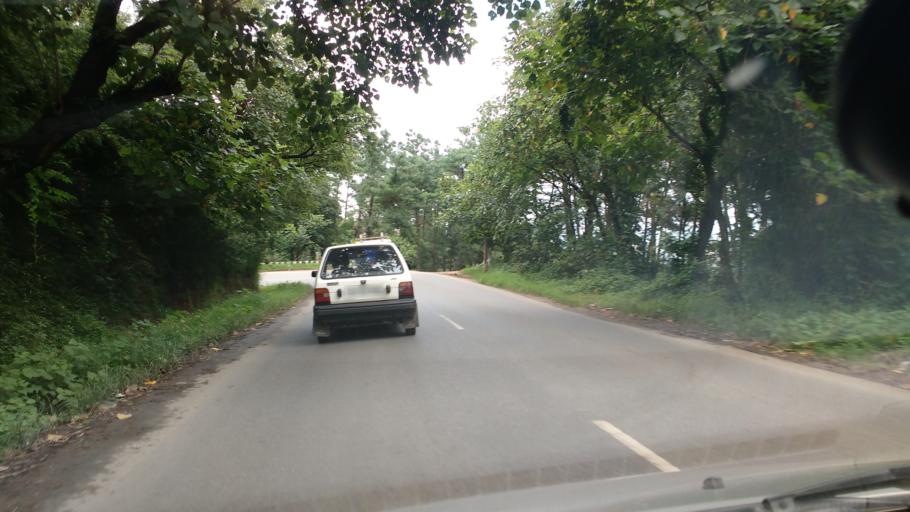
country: IN
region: Meghalaya
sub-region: East Khasi Hills
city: Shillong
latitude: 25.5609
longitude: 91.8530
